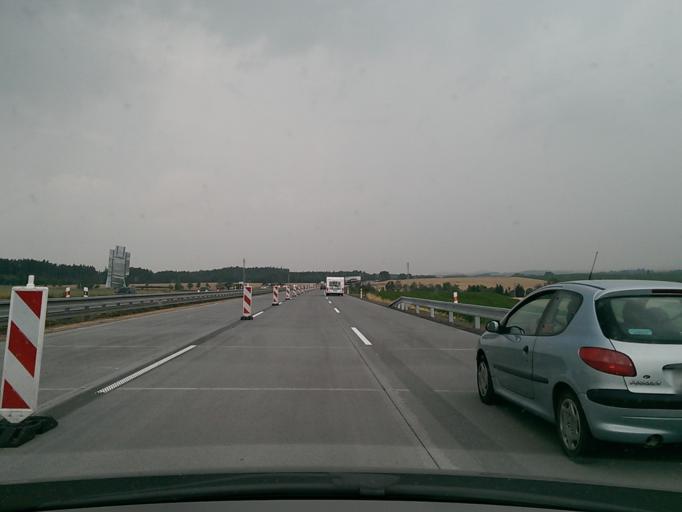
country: CZ
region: Vysocina
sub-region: Okres Zd'ar nad Sazavou
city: Velka Bites
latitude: 49.2780
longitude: 16.2136
